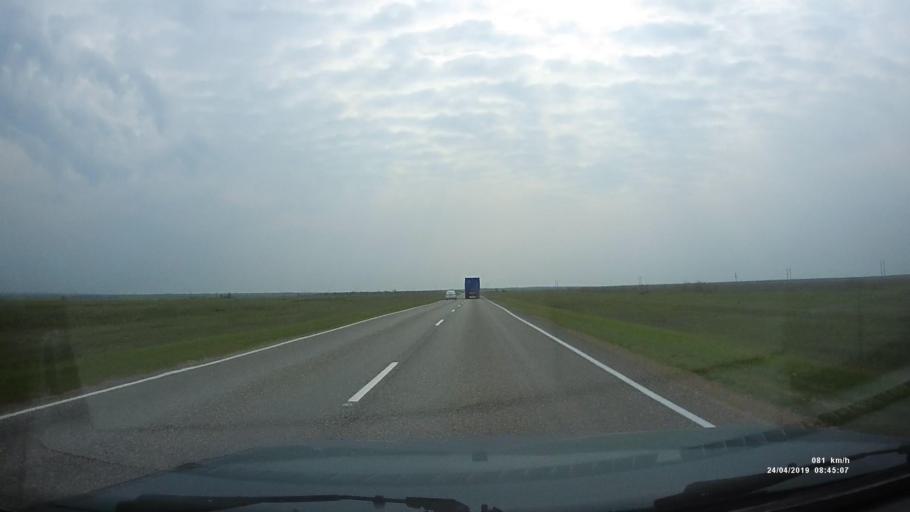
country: RU
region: Kalmykiya
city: Arshan'
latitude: 46.2370
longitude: 44.0552
